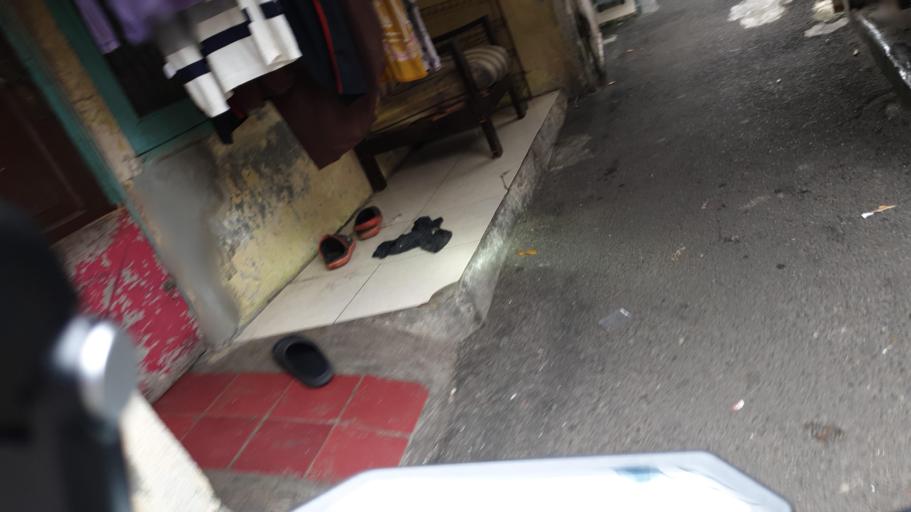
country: ID
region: Banten
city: South Tangerang
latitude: -6.2723
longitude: 106.7933
